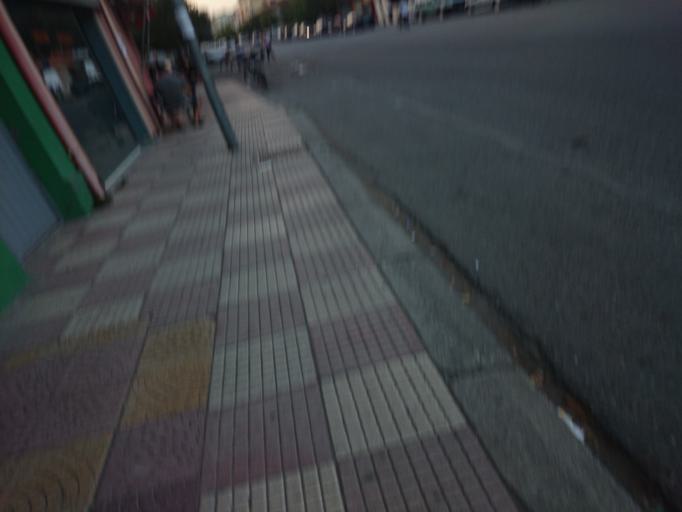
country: AL
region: Shkoder
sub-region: Rrethi i Shkodres
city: Shkoder
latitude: 42.0615
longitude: 19.5211
